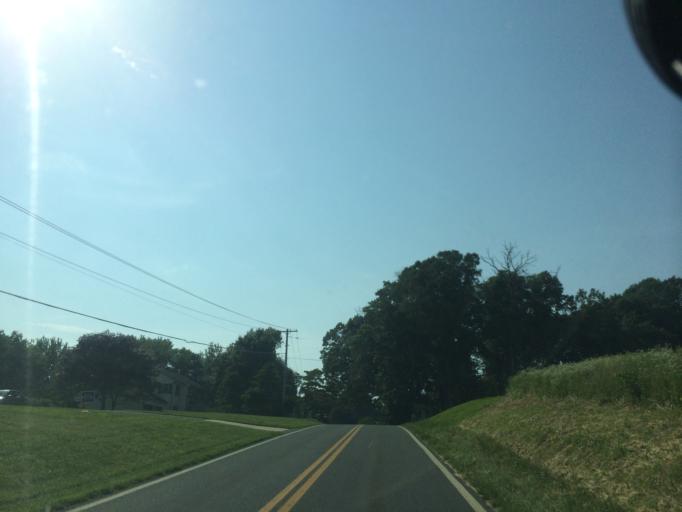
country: US
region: Maryland
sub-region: Carroll County
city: Eldersburg
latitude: 39.4466
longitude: -76.9866
